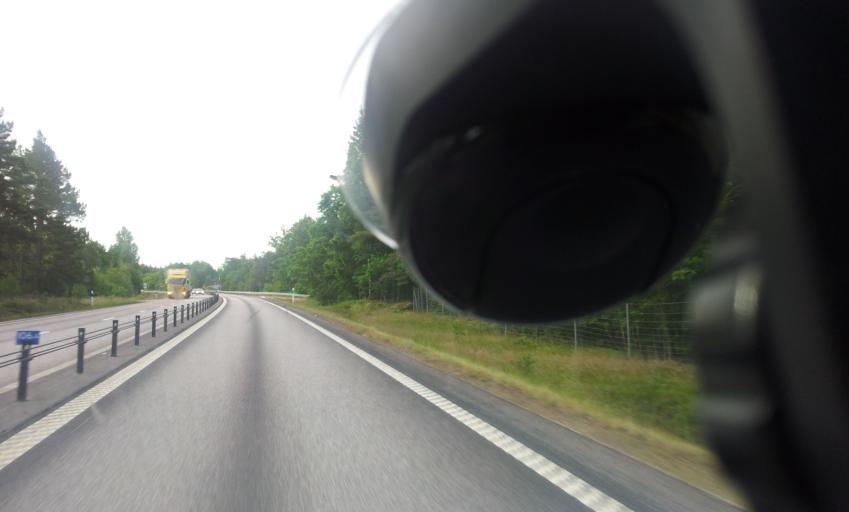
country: SE
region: Kalmar
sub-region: Oskarshamns Kommun
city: Paskallavik
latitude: 57.1320
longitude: 16.4751
